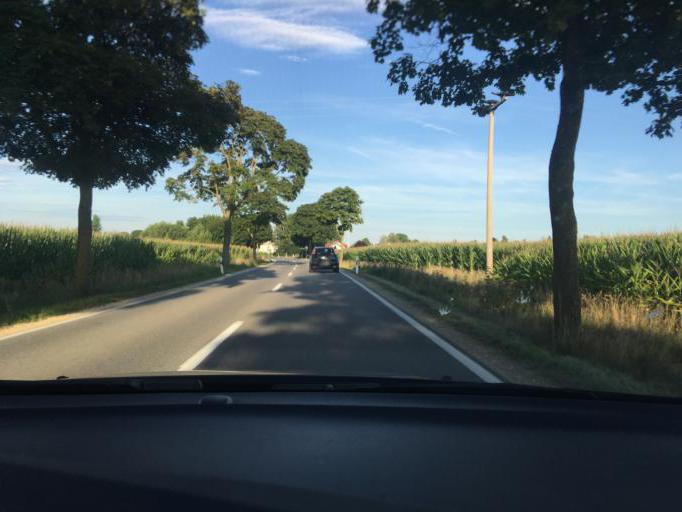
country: DE
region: Bavaria
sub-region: Upper Bavaria
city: Bockhorn
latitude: 48.2899
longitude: 11.9920
